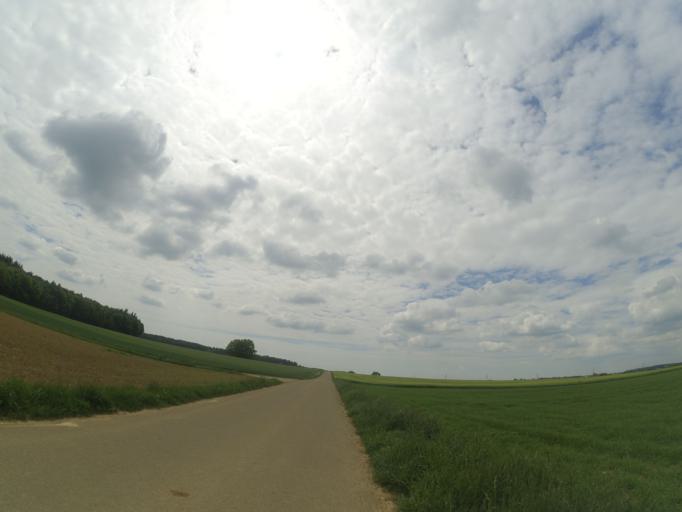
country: DE
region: Baden-Wuerttemberg
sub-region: Tuebingen Region
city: Blaubeuren
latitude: 48.4322
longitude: 9.8292
